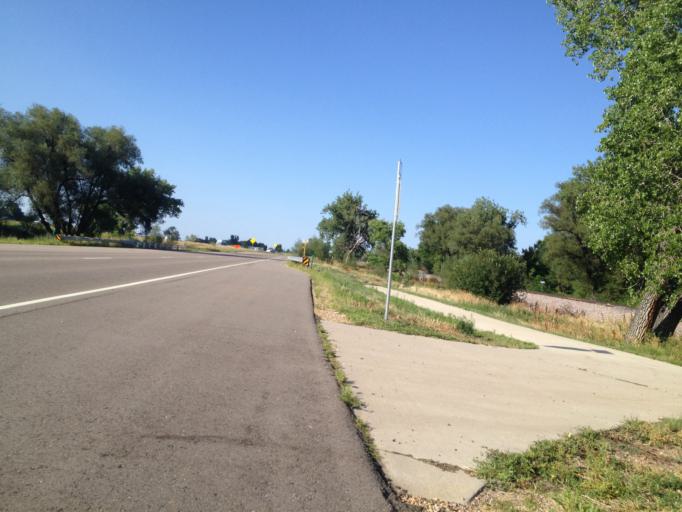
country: US
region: Colorado
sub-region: Boulder County
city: Boulder
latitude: 40.0449
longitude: -105.2394
